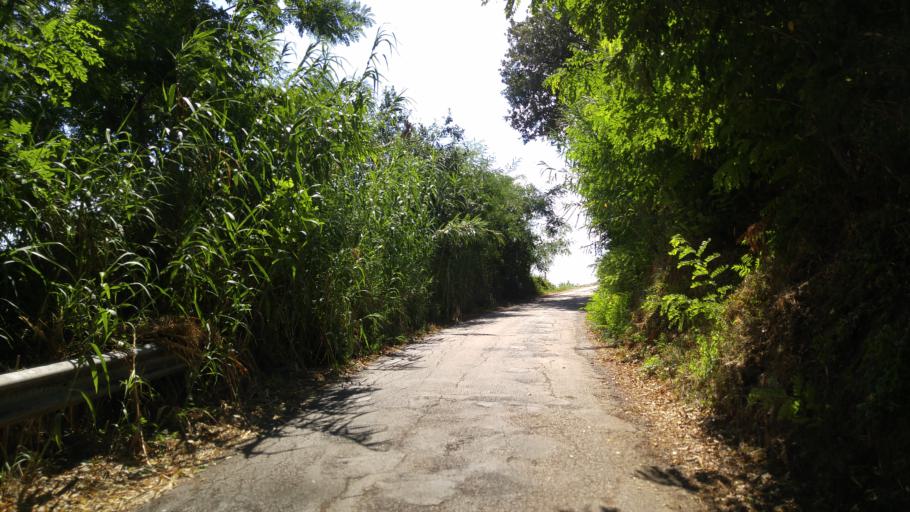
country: IT
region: The Marches
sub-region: Provincia di Pesaro e Urbino
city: Centinarola
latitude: 43.8179
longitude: 12.9794
